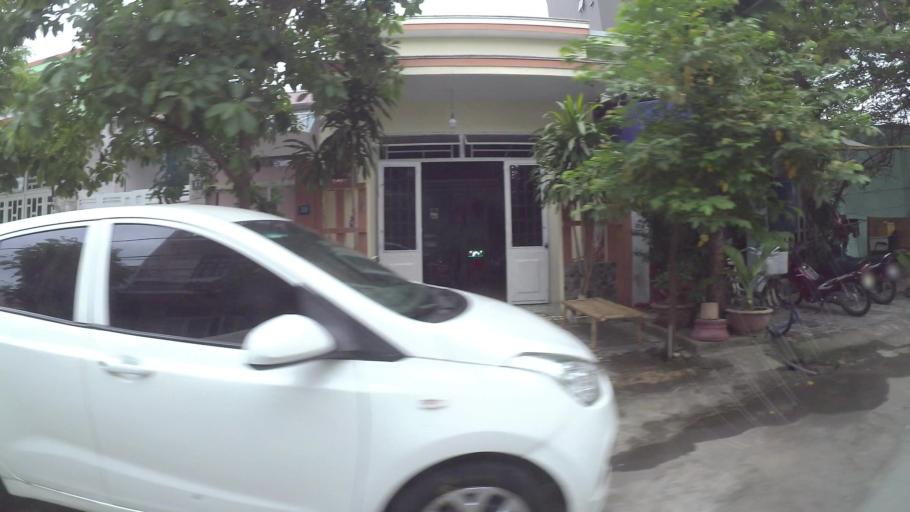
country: VN
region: Da Nang
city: Da Nang
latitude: 16.0976
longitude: 108.2326
